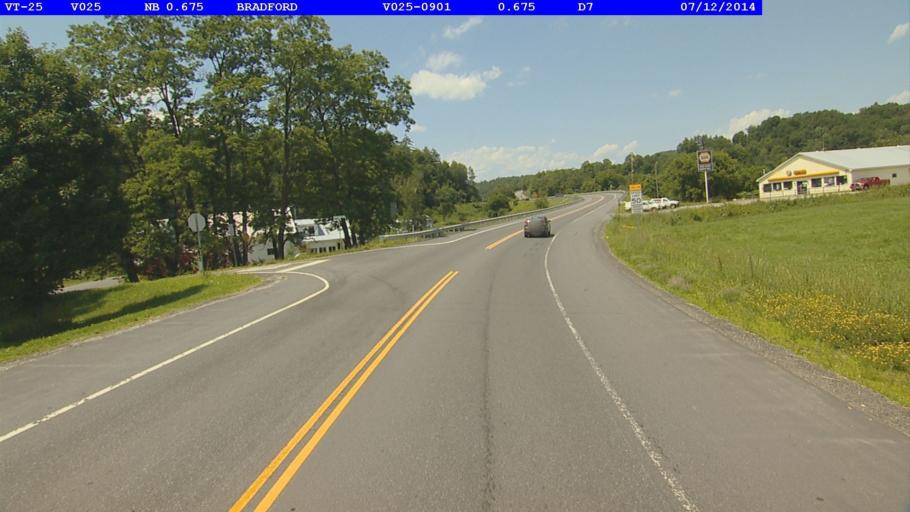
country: US
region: New Hampshire
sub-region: Grafton County
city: Orford
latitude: 43.9821
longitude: -72.1239
